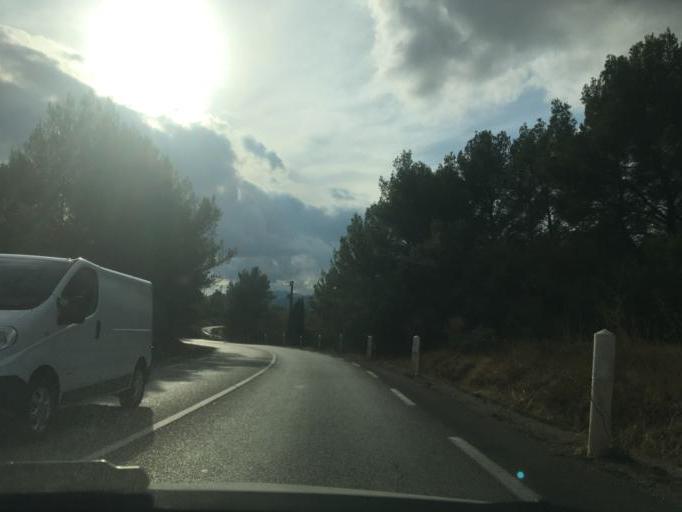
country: FR
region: Provence-Alpes-Cote d'Azur
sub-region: Departement du Var
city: Puget-Ville
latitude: 43.2776
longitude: 6.1238
